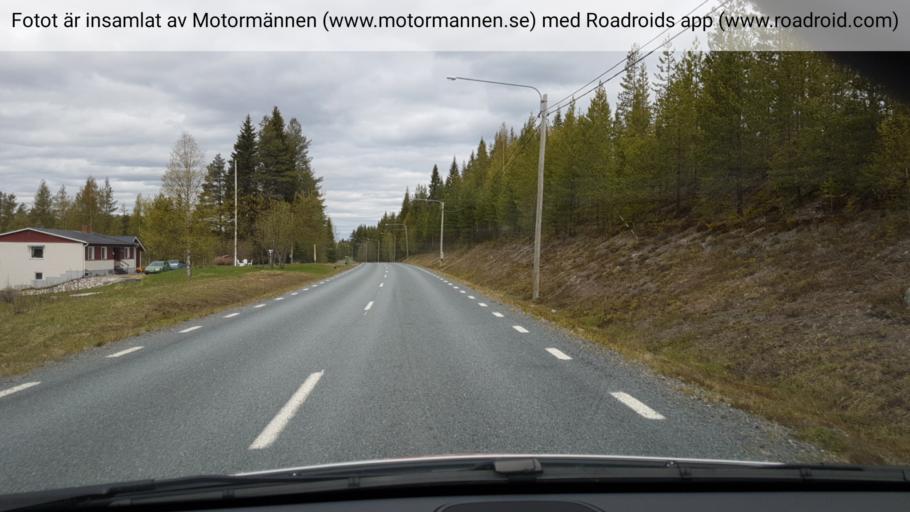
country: SE
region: Vaesterbotten
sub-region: Lycksele Kommun
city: Soderfors
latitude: 65.1166
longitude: 18.2944
